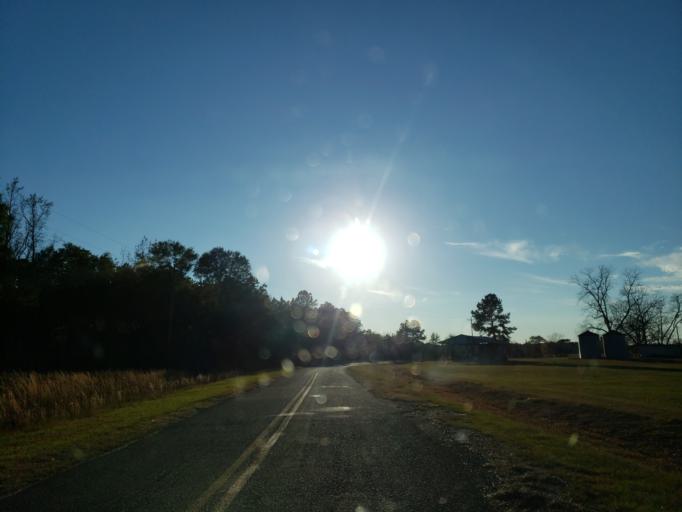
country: US
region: Georgia
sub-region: Dooly County
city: Unadilla
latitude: 32.2084
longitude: -83.7898
